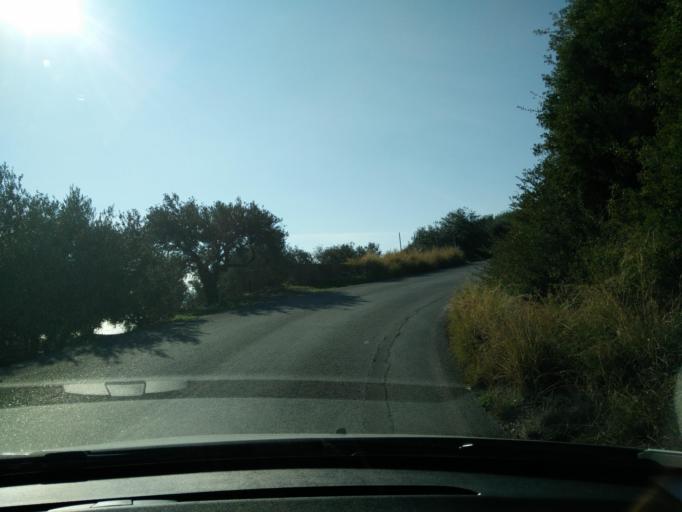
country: GR
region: Crete
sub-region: Nomos Lasithiou
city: Gra Liyia
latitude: 34.9955
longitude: 25.5217
